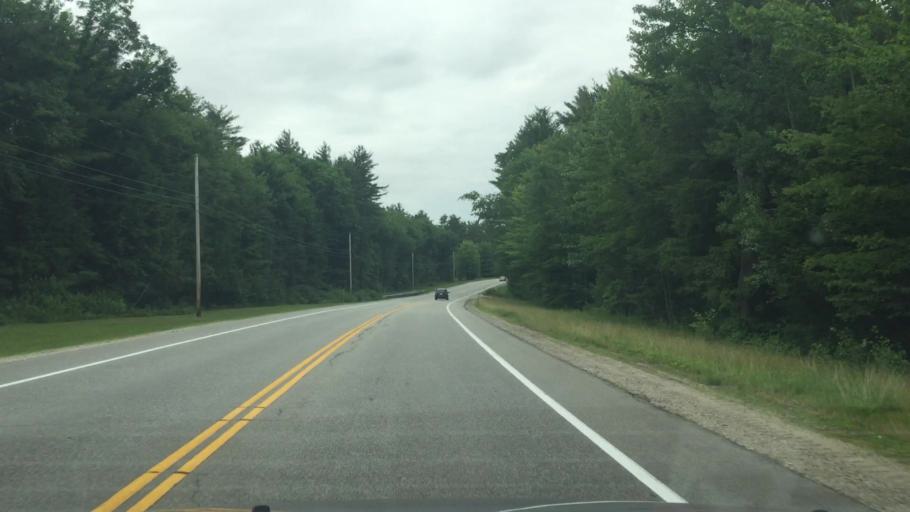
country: US
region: New Hampshire
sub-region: Carroll County
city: Moultonborough
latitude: 43.7743
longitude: -71.3822
